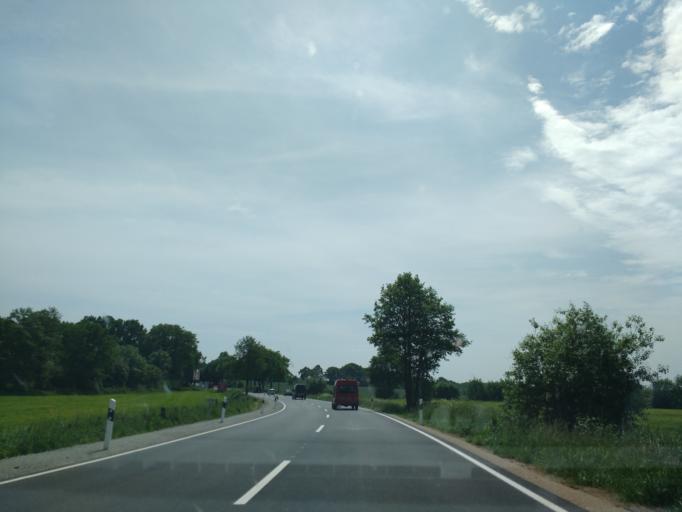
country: DE
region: Schleswig-Holstein
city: Braak
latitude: 53.6042
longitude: 10.2412
